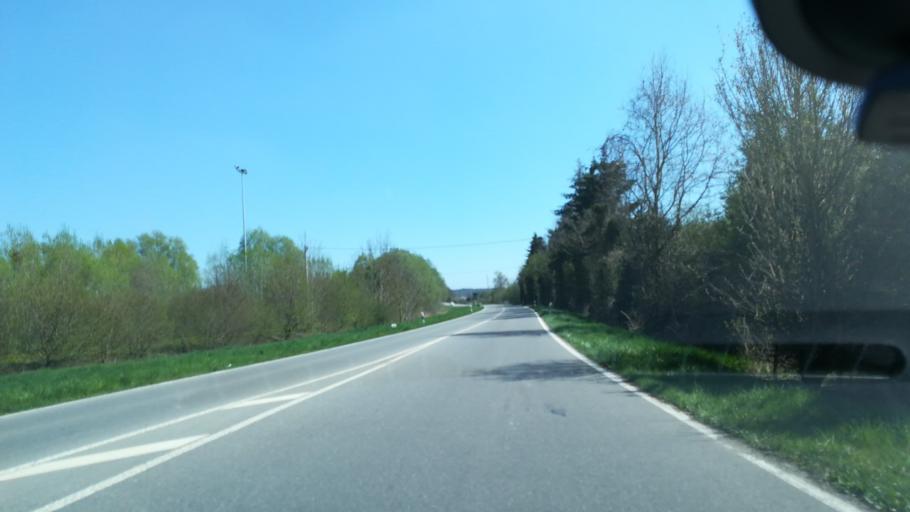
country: DE
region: Baden-Wuerttemberg
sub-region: Freiburg Region
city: Muhlhausen-Ehingen
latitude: 47.8019
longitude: 8.8310
